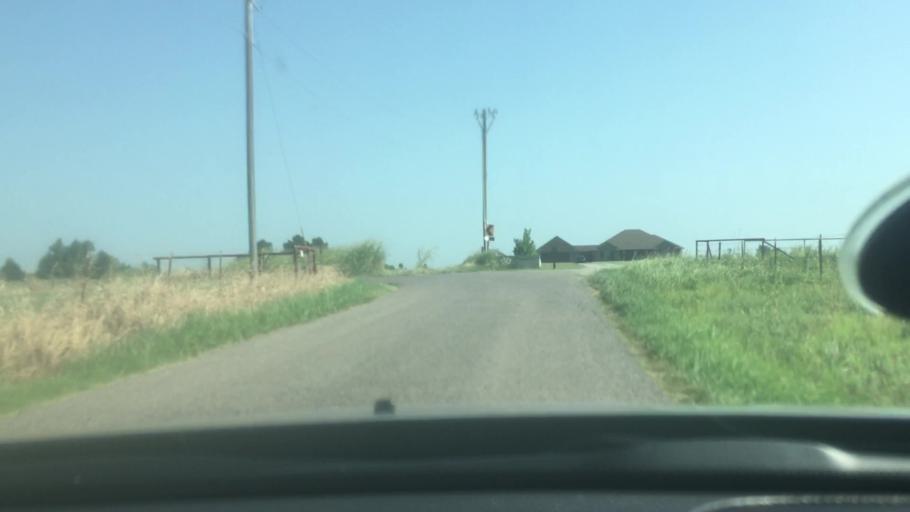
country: US
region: Oklahoma
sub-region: Bryan County
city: Calera
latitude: 33.9542
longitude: -96.4612
